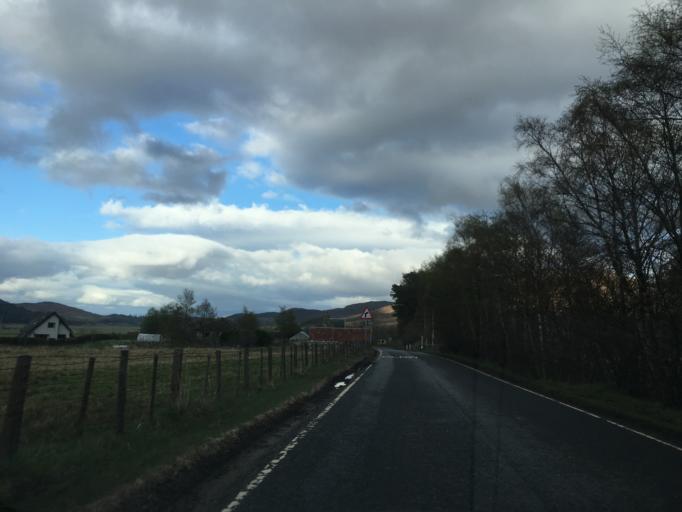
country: GB
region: Scotland
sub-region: Highland
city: Kingussie
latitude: 57.0072
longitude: -4.2553
